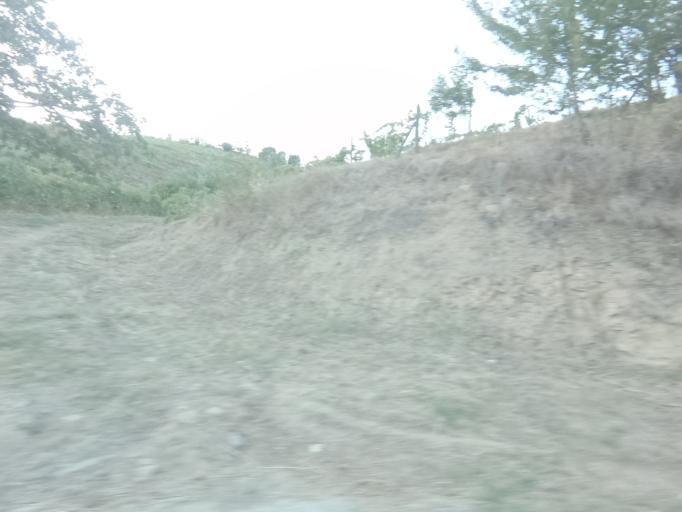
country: PT
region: Vila Real
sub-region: Mesao Frio
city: Mesao Frio
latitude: 41.1800
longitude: -7.8563
